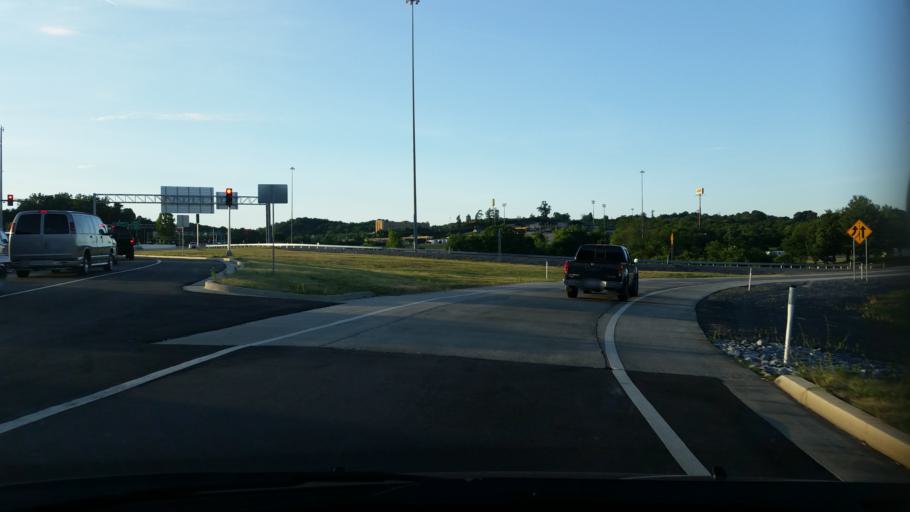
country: US
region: Tennessee
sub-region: Sevier County
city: Sevierville
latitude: 35.9815
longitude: -83.6077
